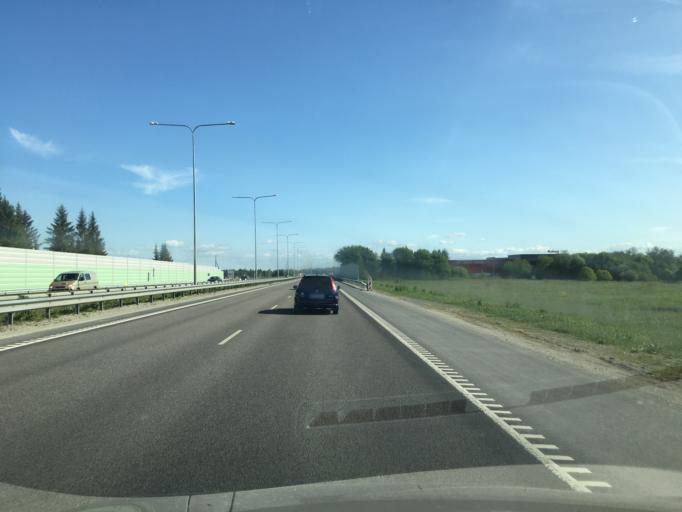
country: EE
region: Harju
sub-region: Rae vald
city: Jueri
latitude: 59.3871
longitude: 24.8317
